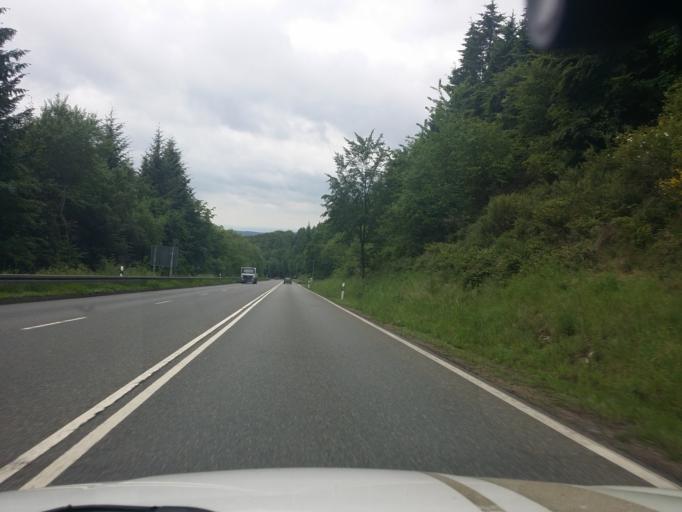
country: DE
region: Hesse
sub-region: Regierungsbezirk Darmstadt
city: Wiesbaden
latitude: 50.1303
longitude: 8.2125
